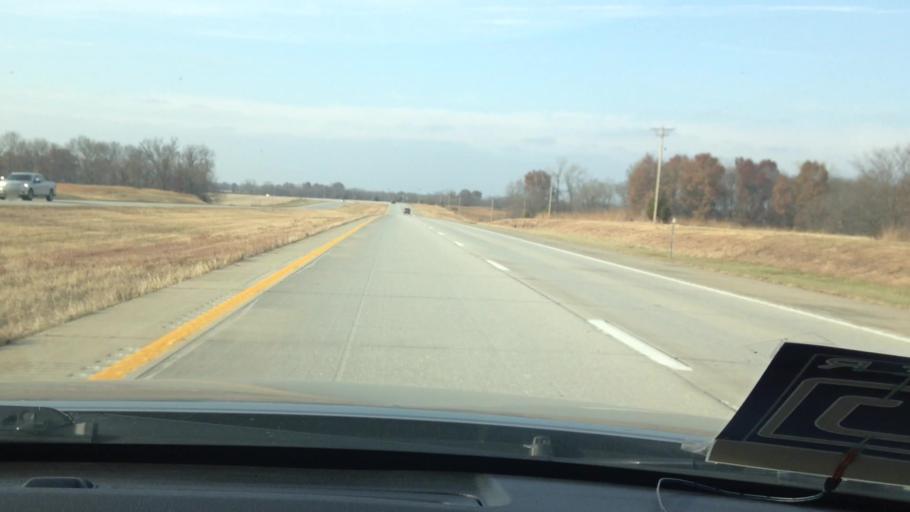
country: US
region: Missouri
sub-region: Henry County
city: Clinton
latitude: 38.4578
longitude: -93.9659
